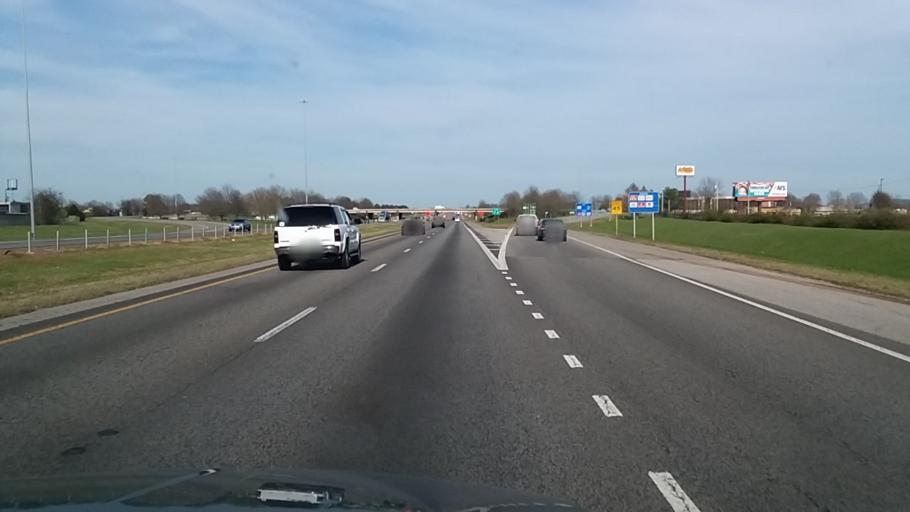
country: US
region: Alabama
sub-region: Madison County
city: Madison
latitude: 34.6712
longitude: -86.7575
